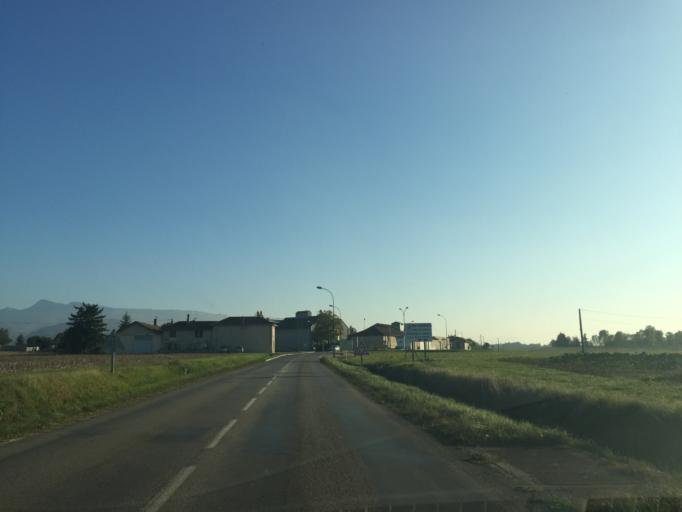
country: FR
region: Rhone-Alpes
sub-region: Departement de la Drome
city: Chatuzange-le-Goubet
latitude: 44.9906
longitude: 5.1022
